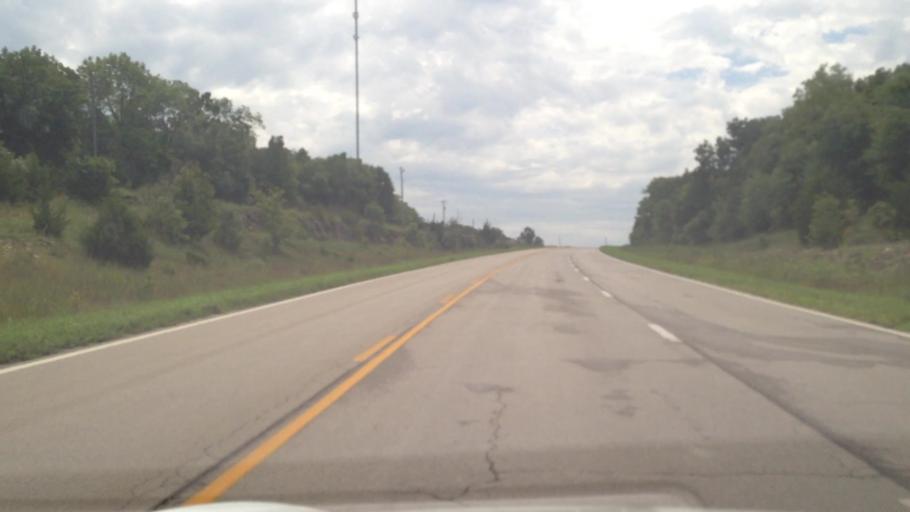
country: US
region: Kansas
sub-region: Bourbon County
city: Fort Scott
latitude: 37.8305
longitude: -94.9802
